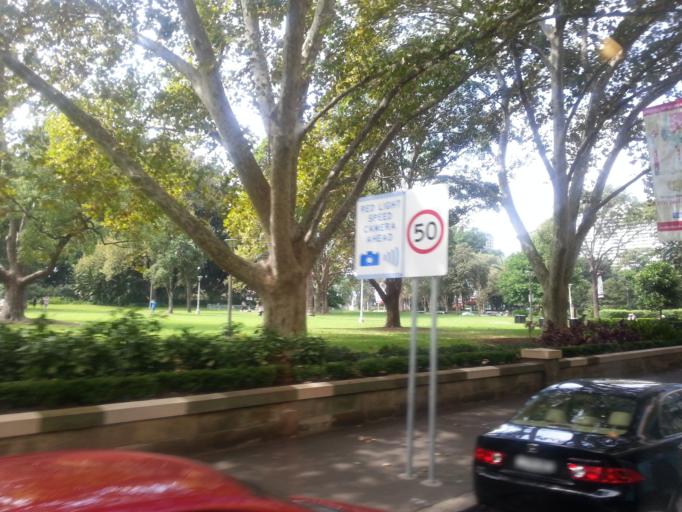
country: AU
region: New South Wales
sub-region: City of Sydney
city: Sydney
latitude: -33.8724
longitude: 151.2105
